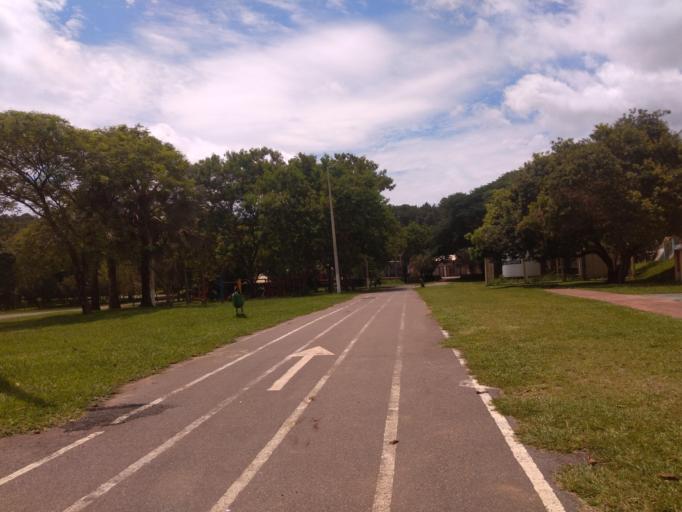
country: BR
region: Minas Gerais
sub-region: Tres Coracoes
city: Tres Coracoes
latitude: -21.7016
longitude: -45.2450
